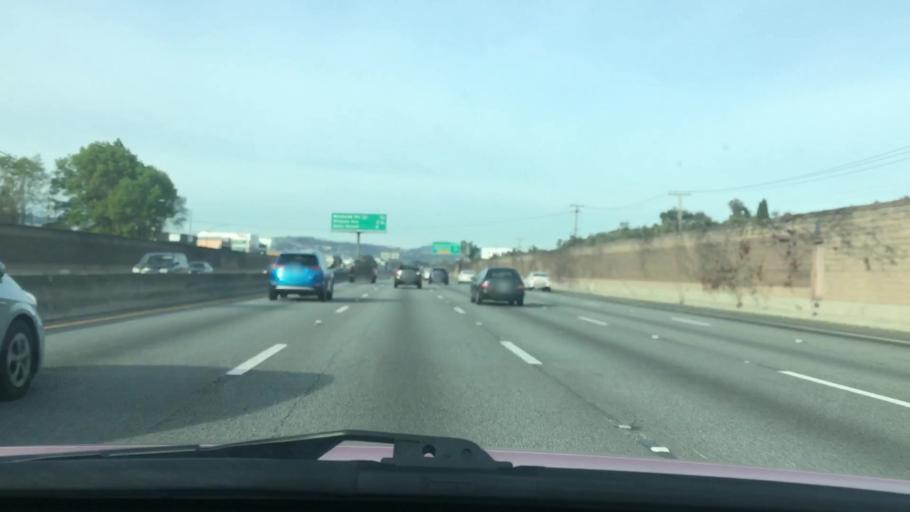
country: US
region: California
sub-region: San Mateo County
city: North Fair Oaks
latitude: 37.4859
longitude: -122.1950
